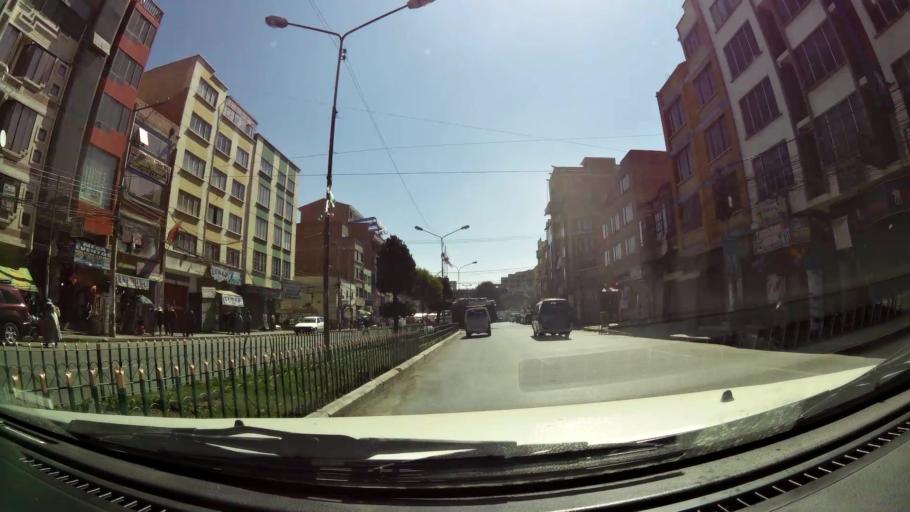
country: BO
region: La Paz
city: La Paz
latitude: -16.4982
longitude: -68.1745
